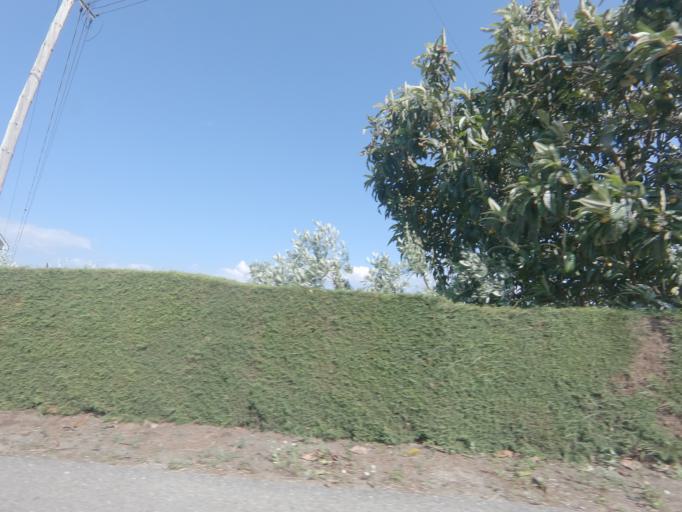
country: PT
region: Vila Real
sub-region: Sabrosa
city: Sabrosa
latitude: 41.2578
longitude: -7.5794
